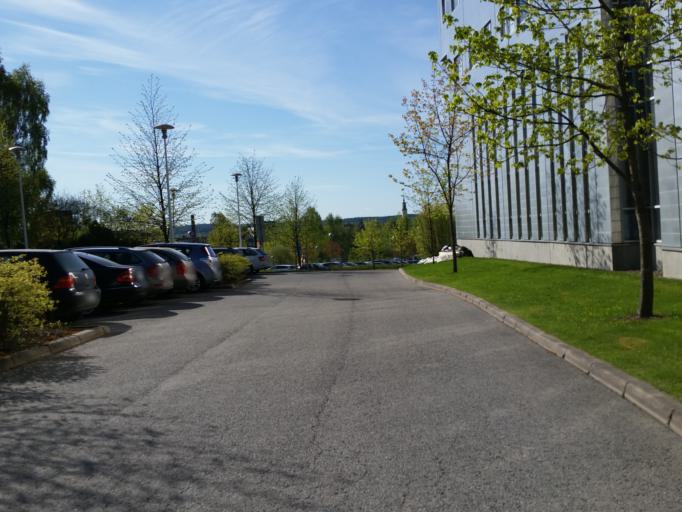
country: FI
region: Pirkanmaa
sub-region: Tampere
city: Tampere
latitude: 61.4932
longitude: 23.7786
